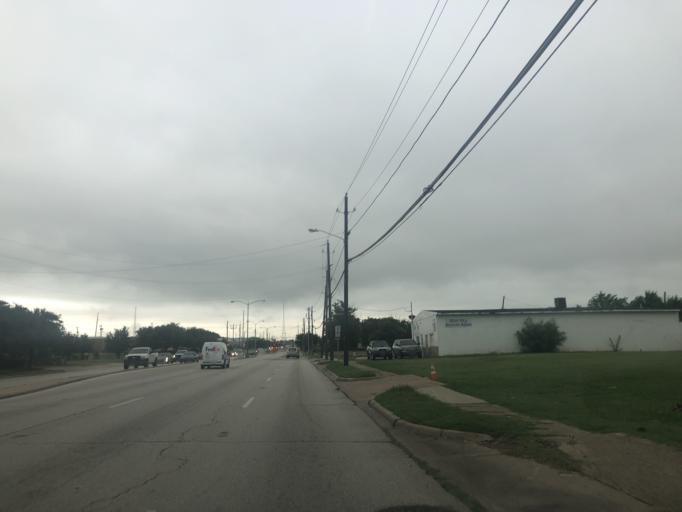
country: US
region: Texas
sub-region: Dallas County
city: Cockrell Hill
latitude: 32.7813
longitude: -96.8739
